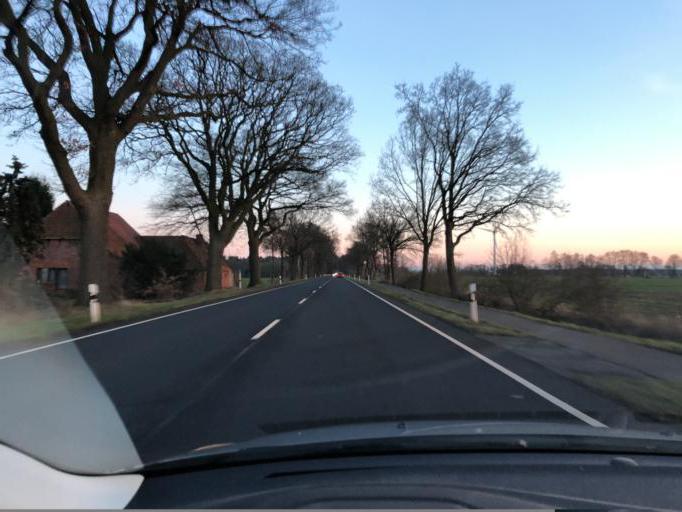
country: DE
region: Lower Saxony
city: Wietzen
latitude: 52.6959
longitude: 9.0881
